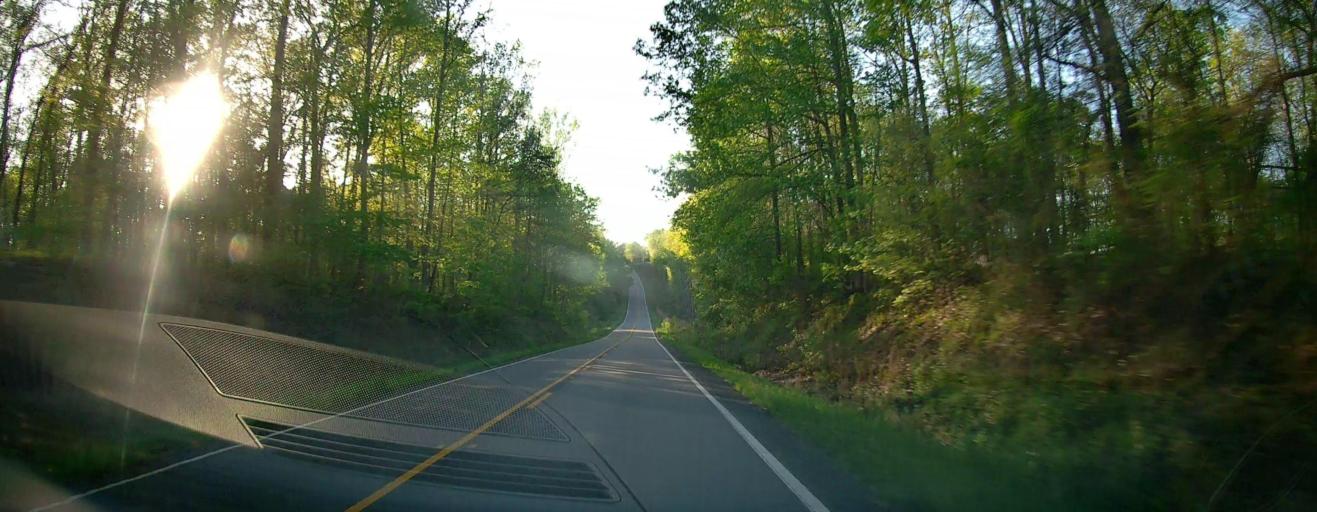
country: US
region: Georgia
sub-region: Schley County
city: Ellaville
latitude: 32.3529
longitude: -84.3821
